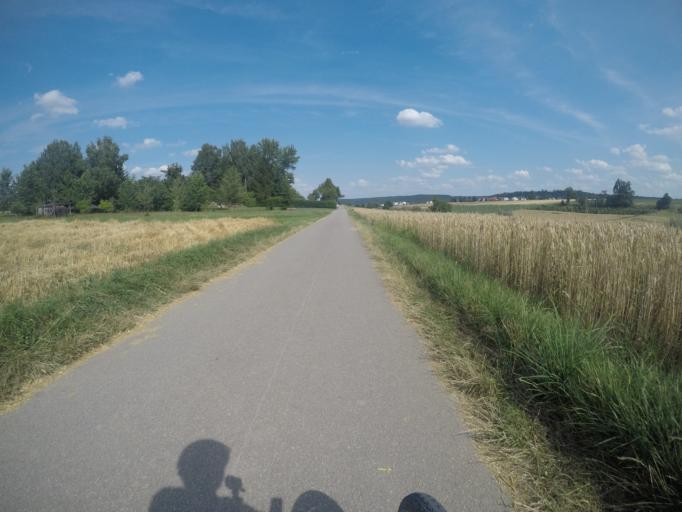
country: DE
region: Baden-Wuerttemberg
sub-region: Regierungsbezirk Stuttgart
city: Nufringen
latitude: 48.6275
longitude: 8.8748
